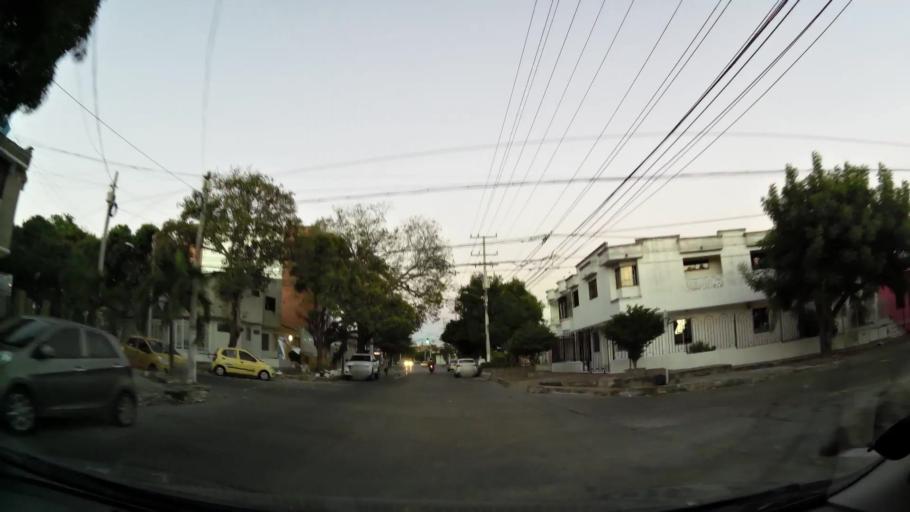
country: CO
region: Atlantico
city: Barranquilla
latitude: 10.9827
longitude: -74.8102
